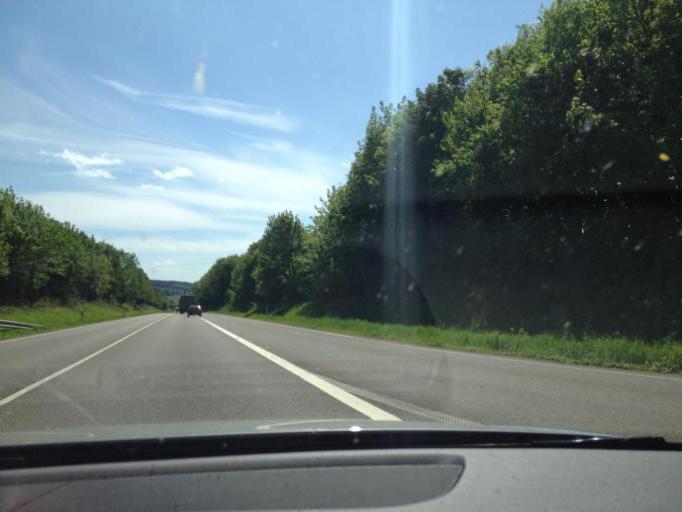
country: DE
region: Rheinland-Pfalz
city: Prum
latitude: 50.1967
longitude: 6.4317
